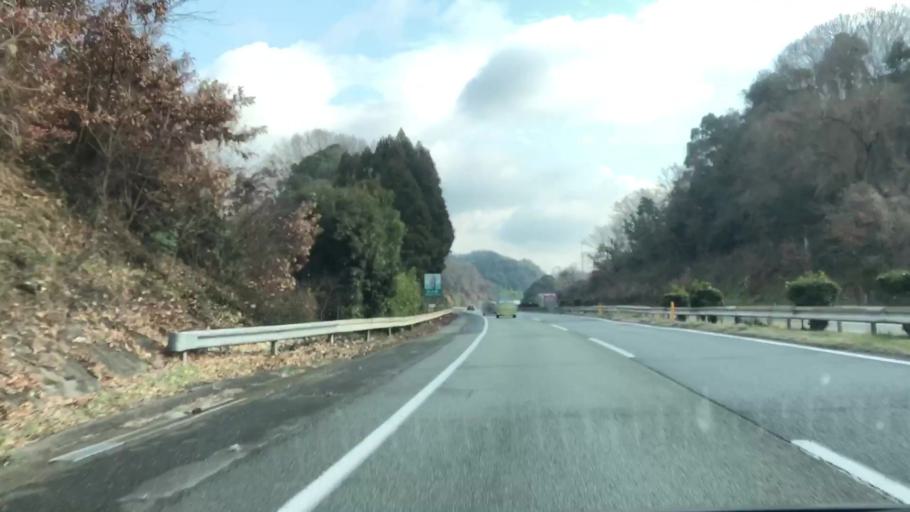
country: JP
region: Kumamoto
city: Tamana
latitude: 33.0027
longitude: 130.5858
